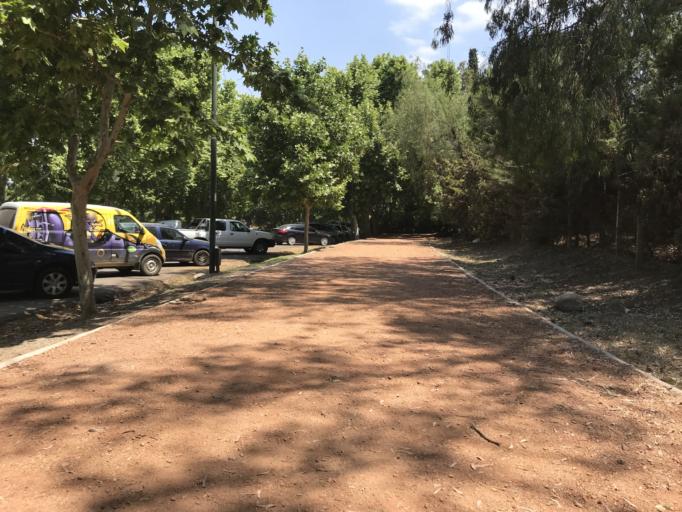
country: AR
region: Mendoza
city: Mendoza
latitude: -32.8969
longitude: -68.8678
